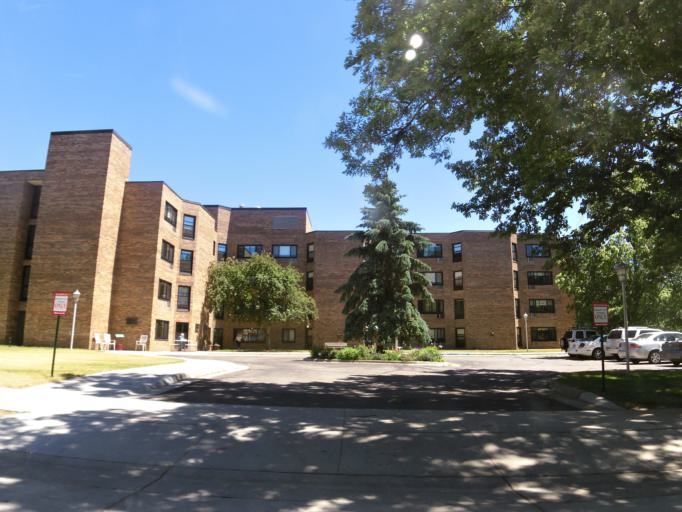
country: US
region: Minnesota
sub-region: Becker County
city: Detroit Lakes
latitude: 46.8130
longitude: -95.8456
